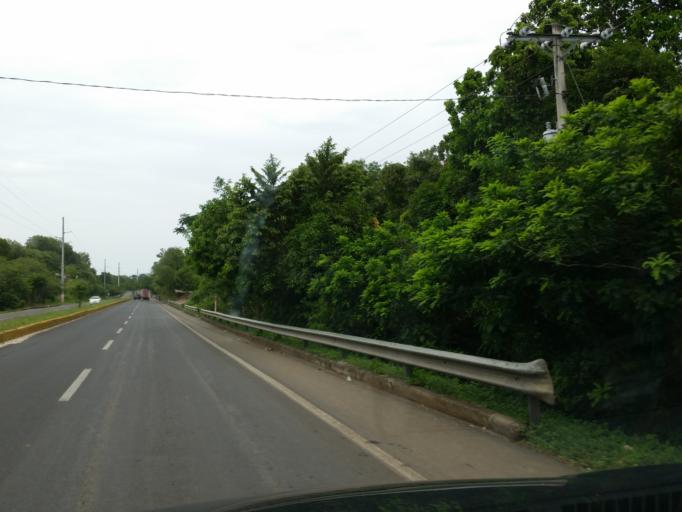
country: NI
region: Masaya
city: Masaya
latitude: 11.9756
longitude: -86.0424
